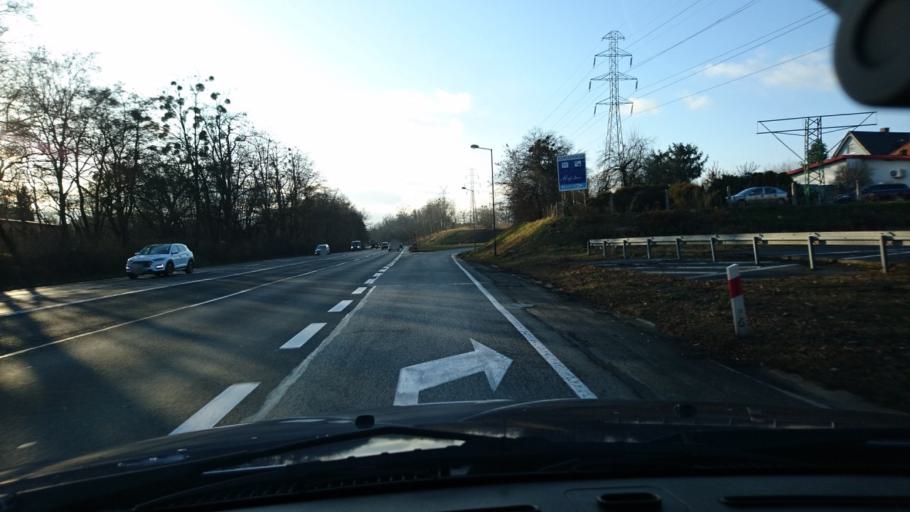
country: PL
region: Silesian Voivodeship
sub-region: Gliwice
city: Gliwice
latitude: 50.3161
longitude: 18.6774
